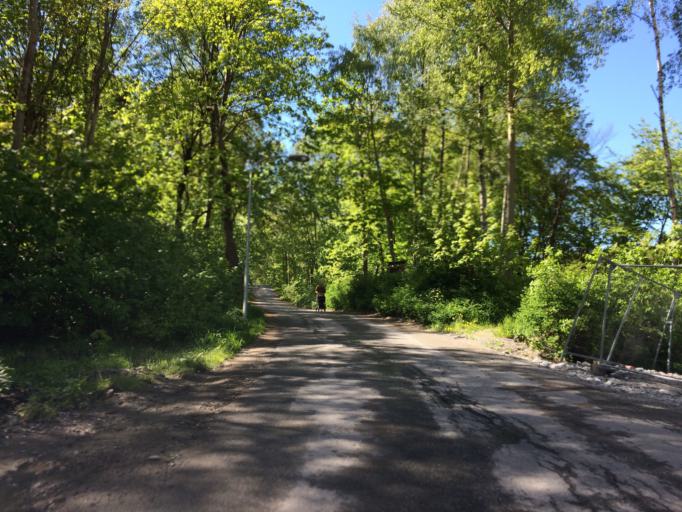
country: SE
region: Stockholm
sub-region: Stockholms Kommun
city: Arsta
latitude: 59.3109
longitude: 18.0057
